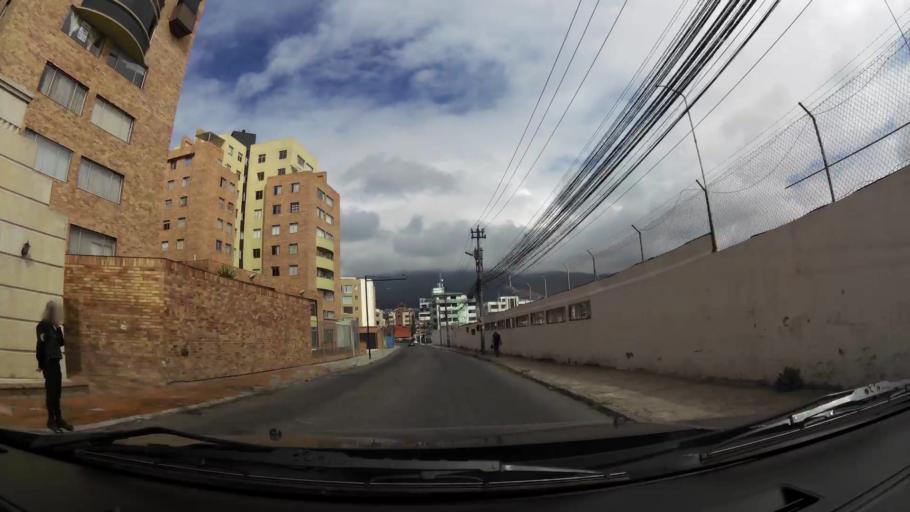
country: EC
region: Pichincha
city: Quito
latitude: -0.1692
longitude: -78.4769
